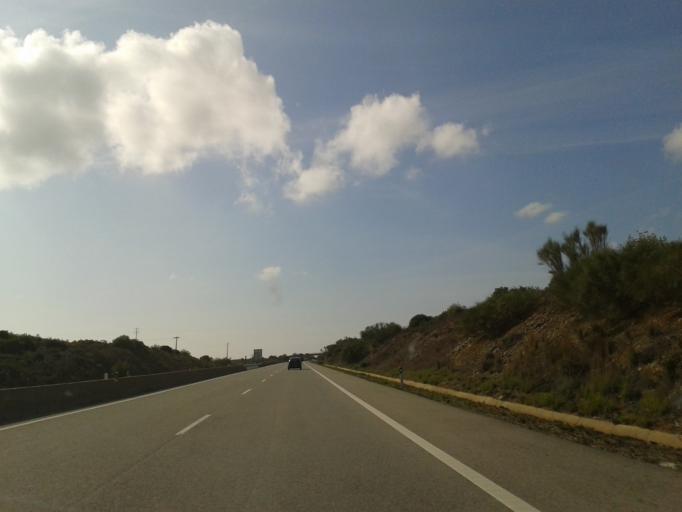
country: PT
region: Faro
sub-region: Olhao
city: Moncarapacho
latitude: 37.0953
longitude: -7.8116
